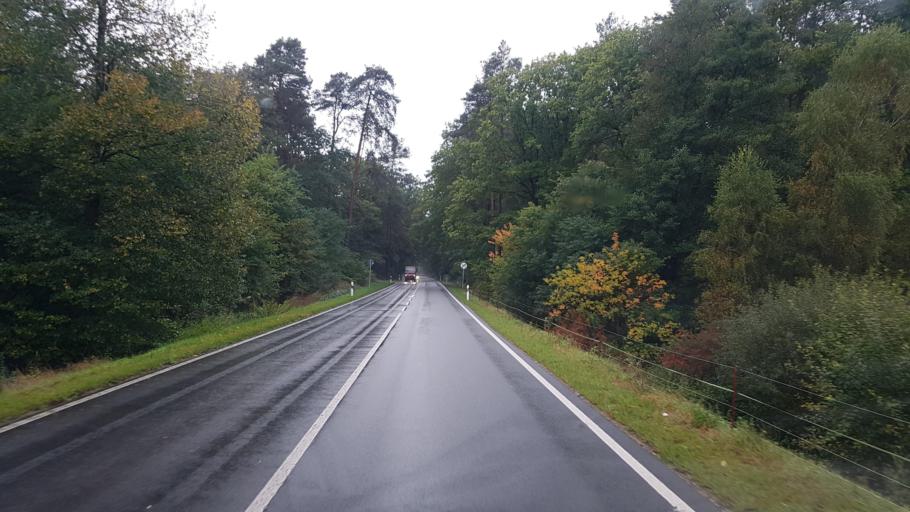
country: DE
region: Brandenburg
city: Bad Saarow
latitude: 52.3008
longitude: 14.0518
